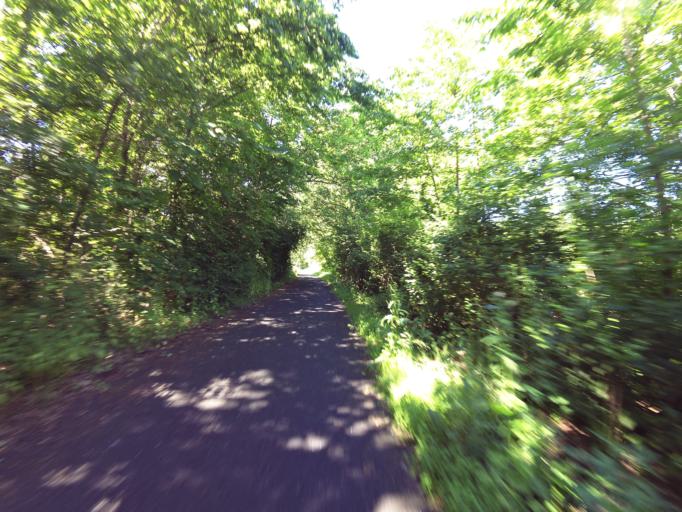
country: DK
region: Capital Region
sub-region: Gladsaxe Municipality
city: Buddinge
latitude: 55.7209
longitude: 12.4945
